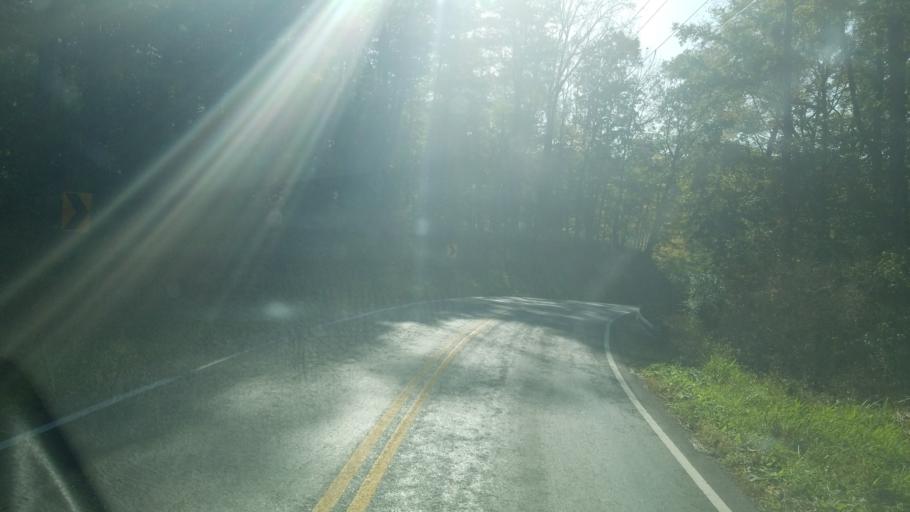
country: US
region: Ohio
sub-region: Wayne County
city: West Salem
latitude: 40.9117
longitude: -82.0044
